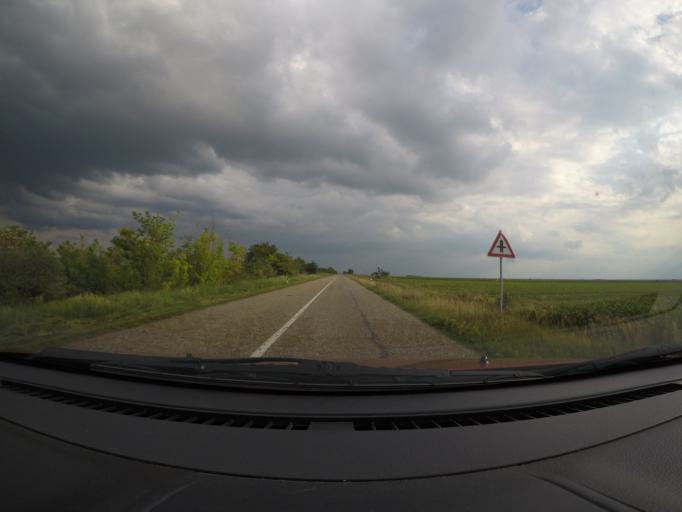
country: RS
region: Autonomna Pokrajina Vojvodina
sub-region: Juznobanatski Okrug
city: Kovacica
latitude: 45.1577
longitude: 20.6170
